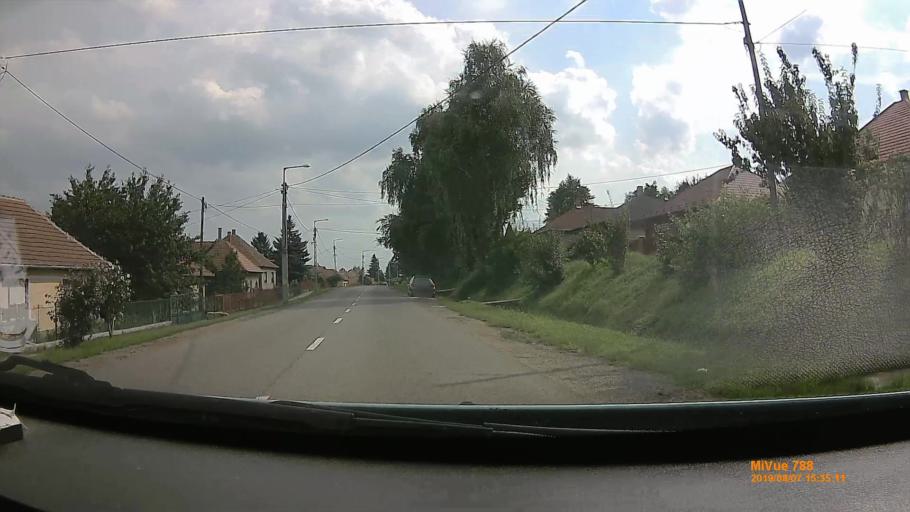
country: HU
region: Borsod-Abauj-Zemplen
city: Encs
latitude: 48.4139
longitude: 21.1738
